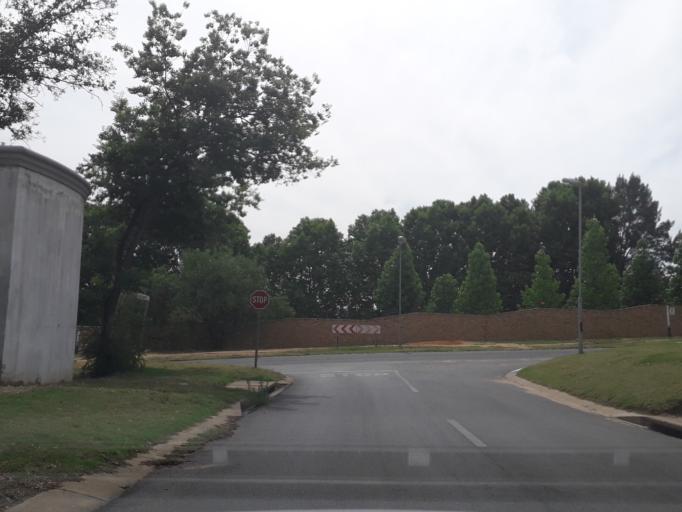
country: ZA
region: Gauteng
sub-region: City of Johannesburg Metropolitan Municipality
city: Diepsloot
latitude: -26.0595
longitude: 28.0137
